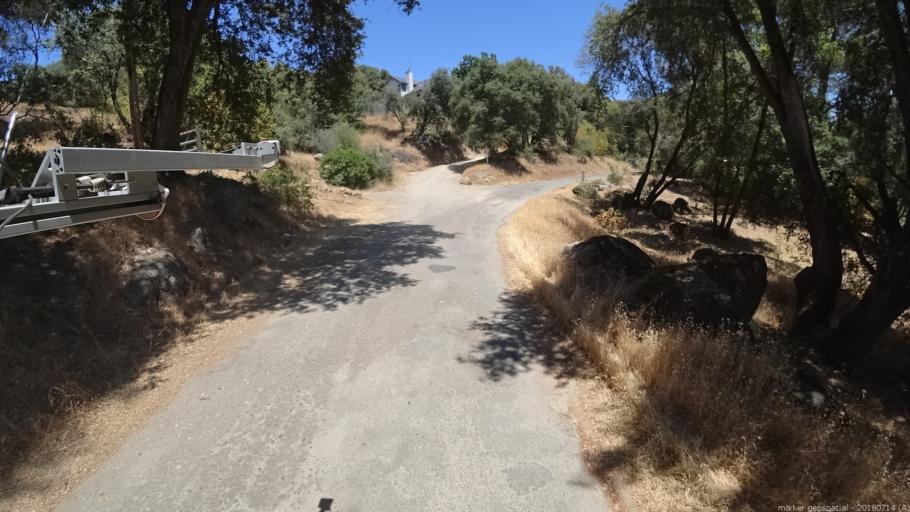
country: US
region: California
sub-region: Madera County
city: Ahwahnee
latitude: 37.4155
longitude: -119.7189
